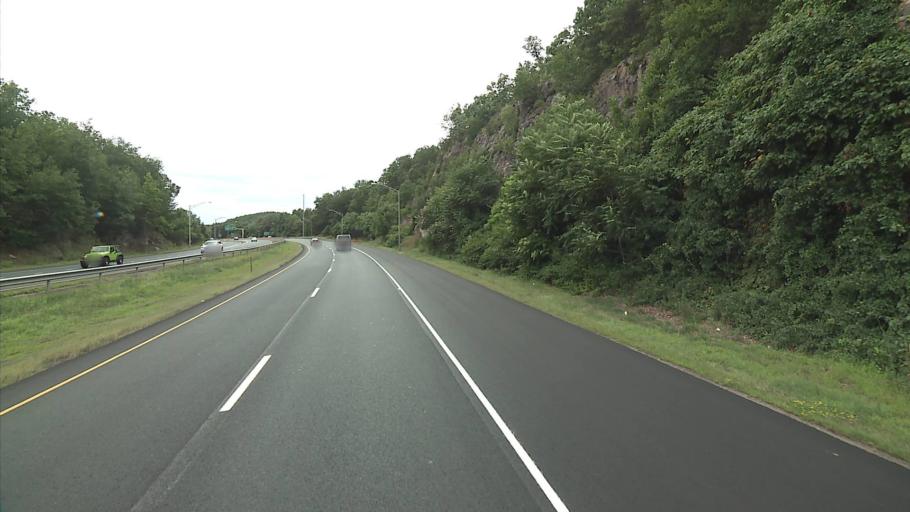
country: US
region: Connecticut
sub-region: New Haven County
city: Naugatuck
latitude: 41.5179
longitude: -73.0492
